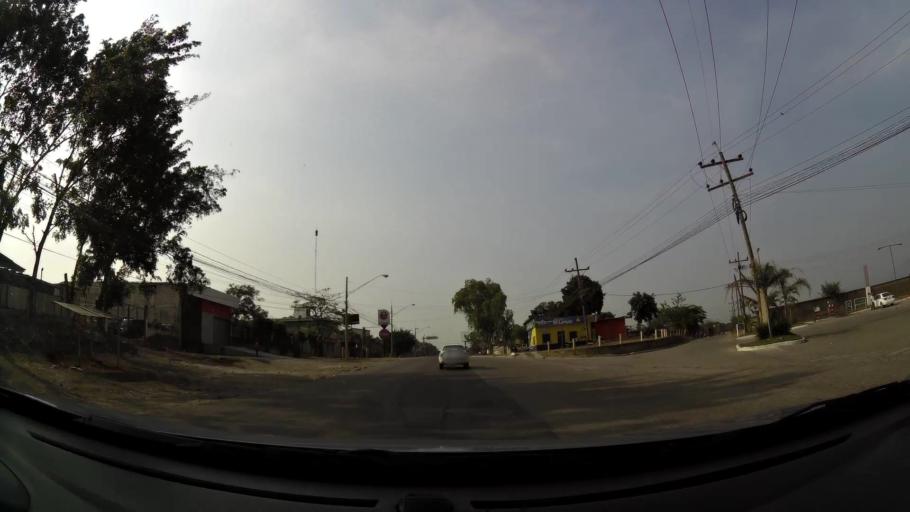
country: HN
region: Comayagua
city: Comayagua
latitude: 14.4417
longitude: -87.6360
